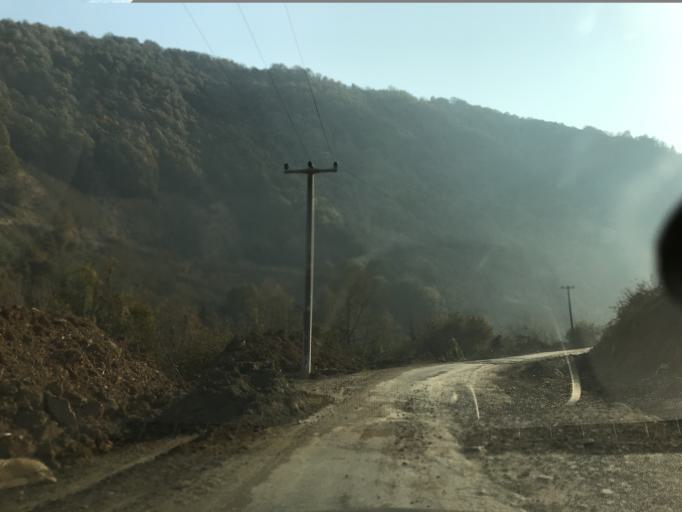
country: TR
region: Duzce
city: Cumayeri
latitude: 40.9285
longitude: 30.9283
